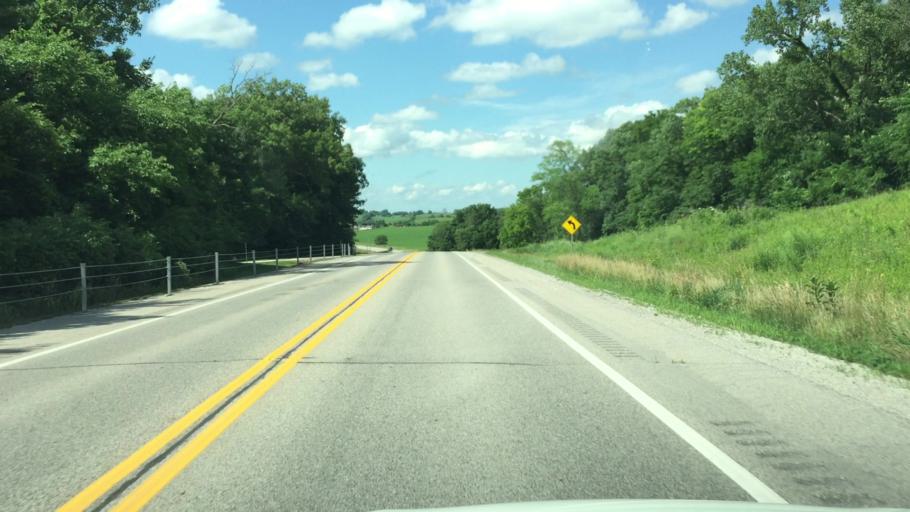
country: US
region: Iowa
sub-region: Johnson County
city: Solon
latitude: 41.7461
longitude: -91.4738
